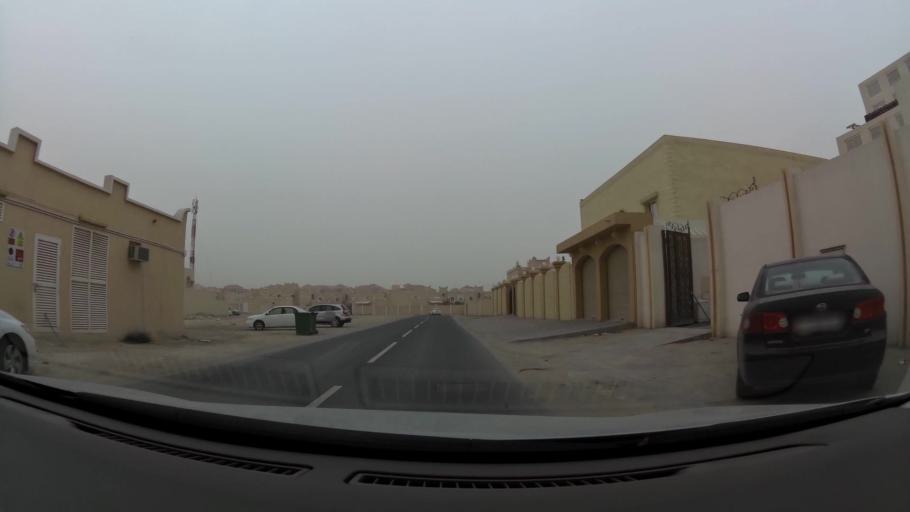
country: QA
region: Baladiyat ad Dawhah
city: Doha
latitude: 25.2437
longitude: 51.4895
